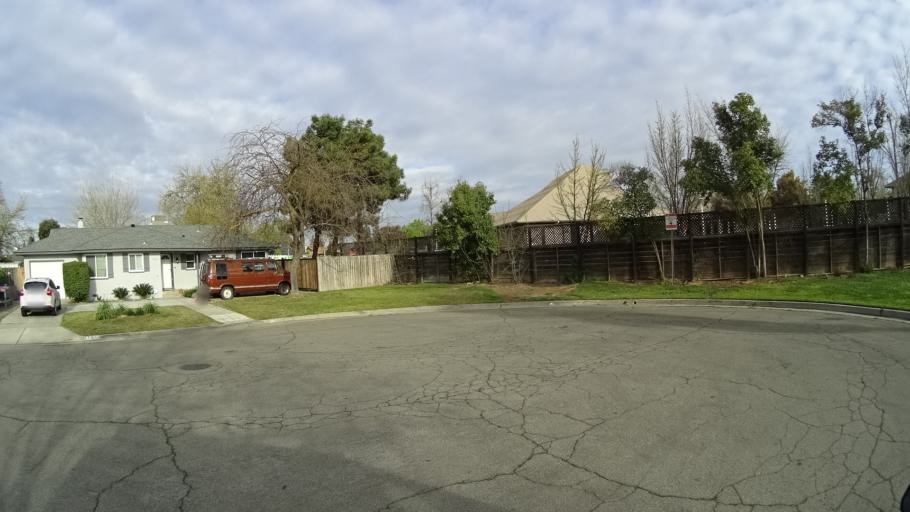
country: US
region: California
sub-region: Fresno County
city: Fresno
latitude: 36.8336
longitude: -119.7980
